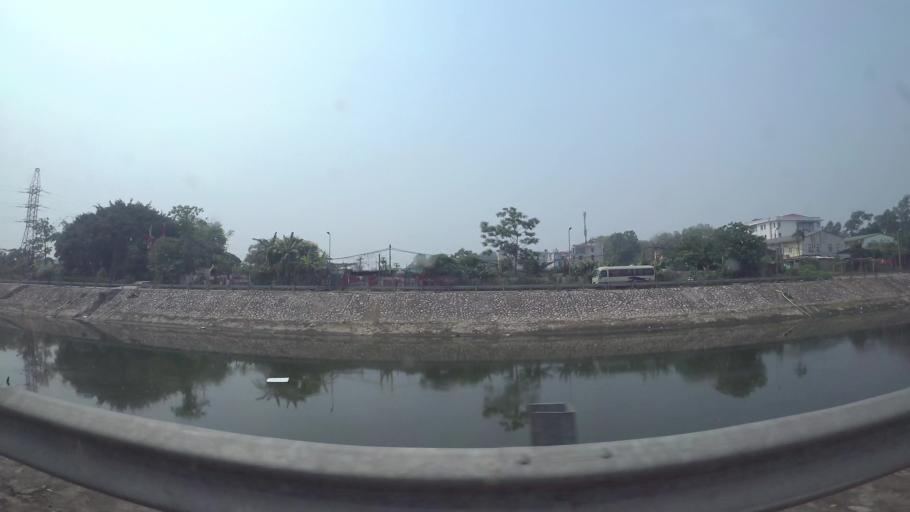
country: VN
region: Ha Noi
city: Van Dien
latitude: 20.9574
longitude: 105.8236
